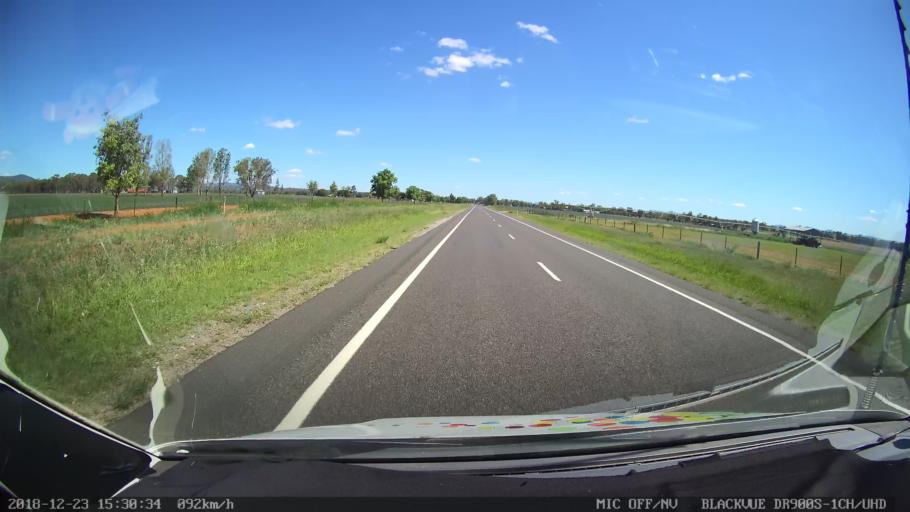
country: AU
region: New South Wales
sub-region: Tamworth Municipality
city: East Tamworth
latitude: -30.9604
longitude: 150.8663
